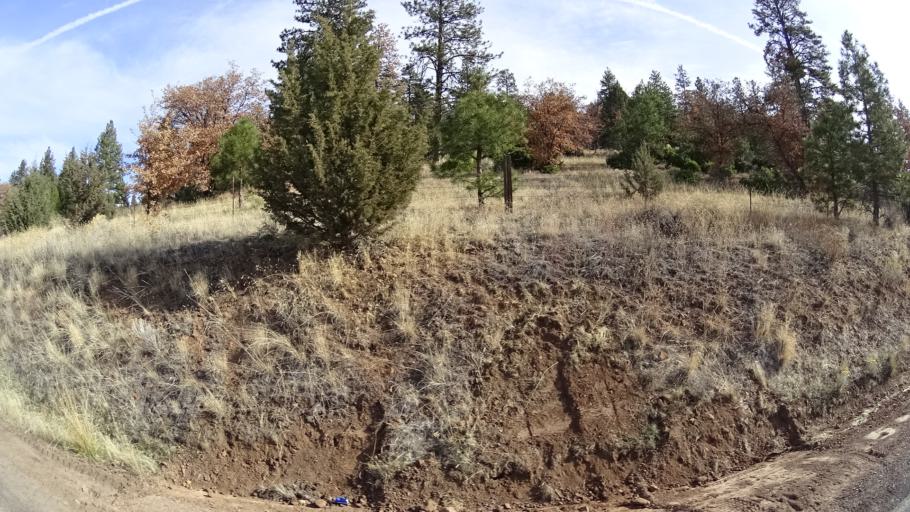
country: US
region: California
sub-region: Siskiyou County
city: Weed
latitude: 41.4713
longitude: -122.4139
